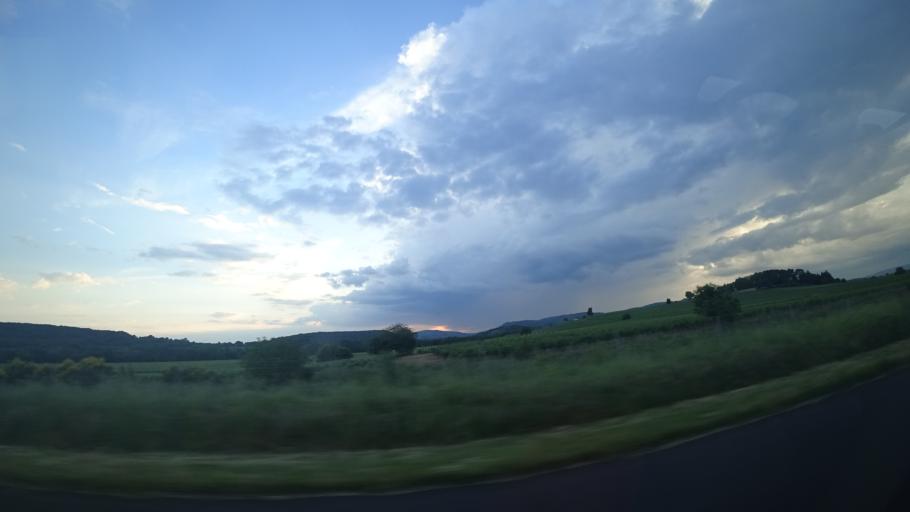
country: FR
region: Languedoc-Roussillon
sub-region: Departement de l'Herault
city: Aspiran
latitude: 43.5886
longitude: 3.4653
